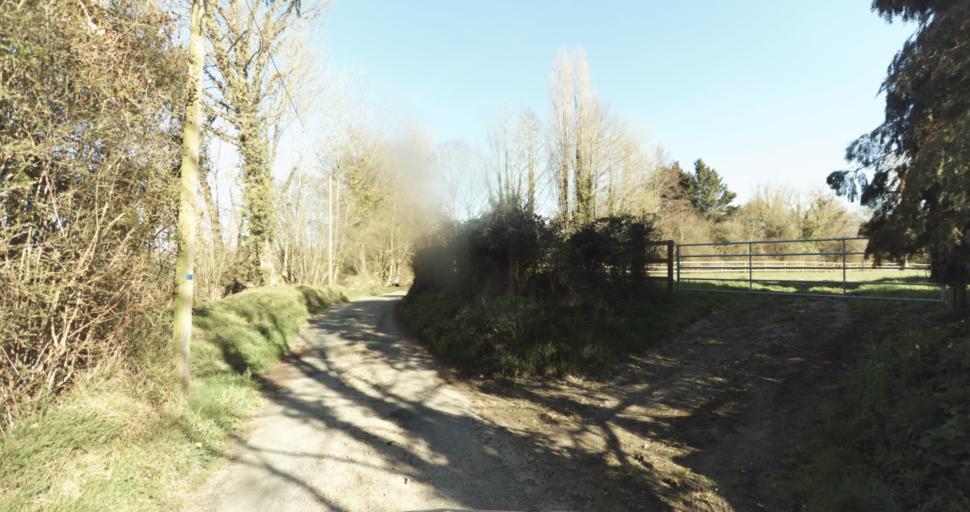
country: FR
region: Lower Normandy
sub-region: Departement du Calvados
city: Livarot
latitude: 49.0374
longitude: 0.0606
